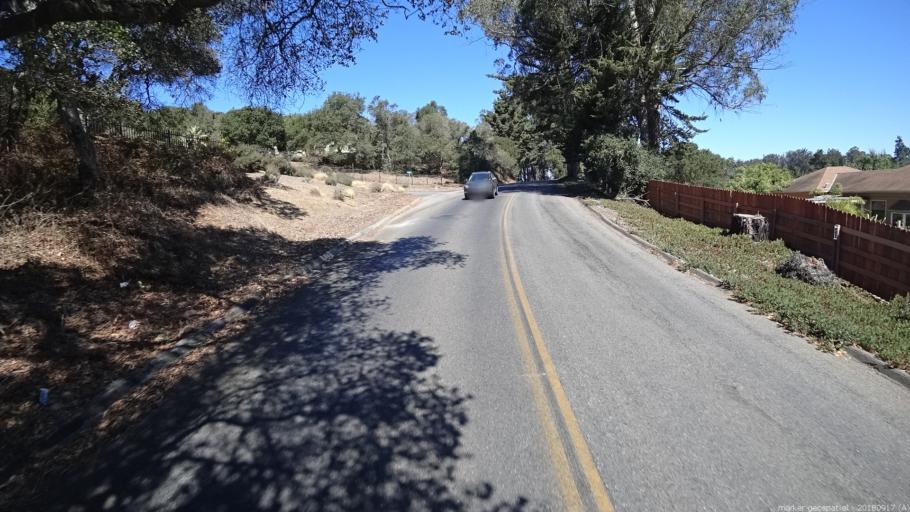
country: US
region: California
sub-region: Monterey County
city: Prunedale
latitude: 36.8307
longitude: -121.6801
